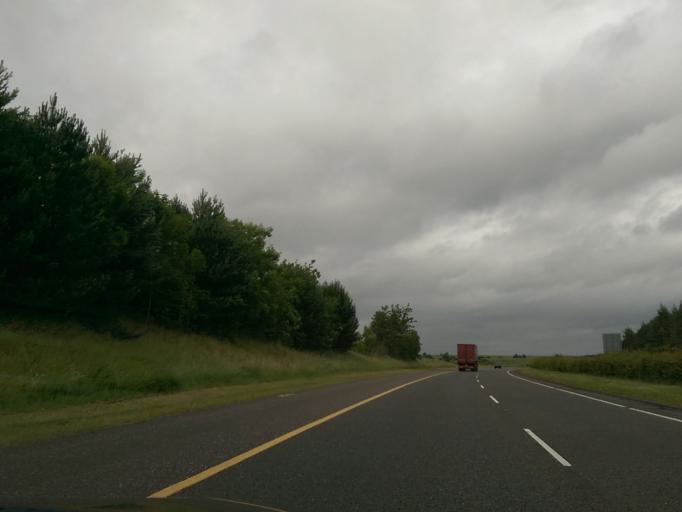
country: IE
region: Munster
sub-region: An Clar
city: Newmarket on Fergus
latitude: 52.7604
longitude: -8.9168
